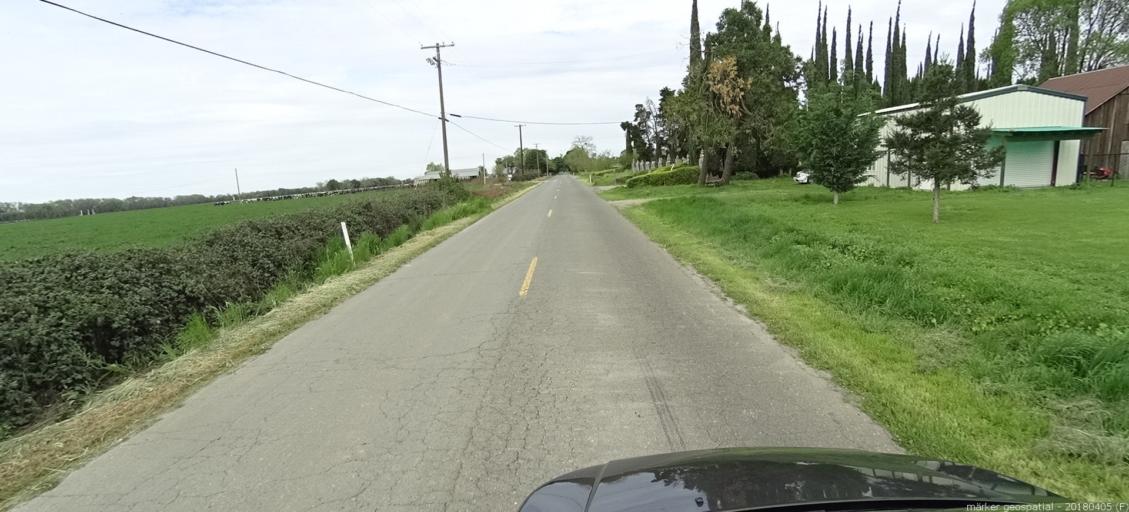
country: US
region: California
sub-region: Sacramento County
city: Galt
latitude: 38.2402
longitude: -121.3195
